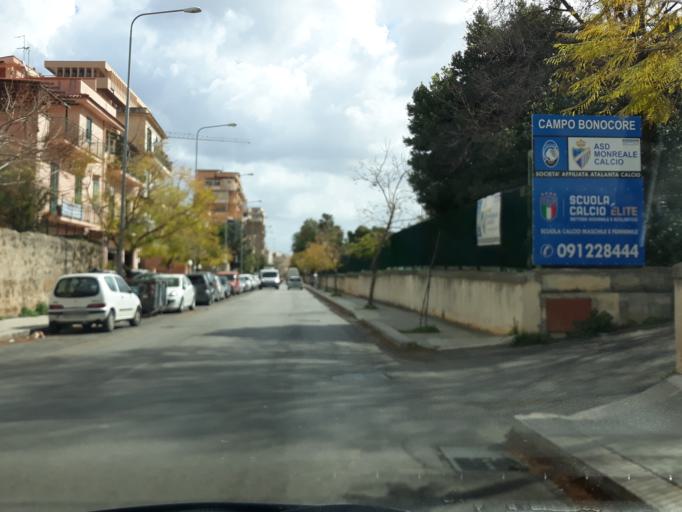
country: IT
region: Sicily
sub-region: Palermo
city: Palermo
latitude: 38.1230
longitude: 13.3224
